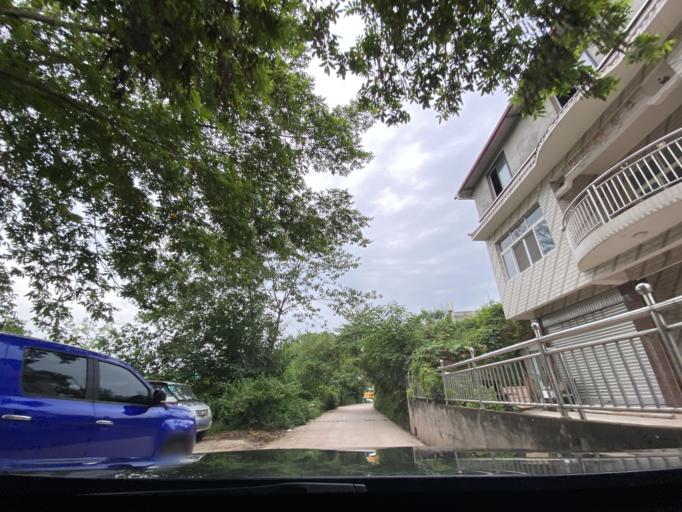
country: CN
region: Sichuan
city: Jiancheng
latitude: 30.3871
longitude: 104.5037
